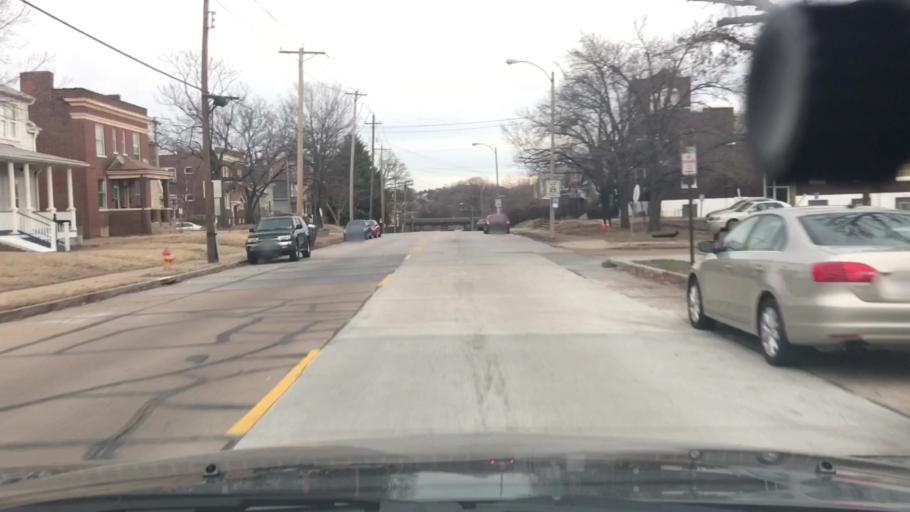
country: US
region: Missouri
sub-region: Saint Louis County
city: Maplewood
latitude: 38.6132
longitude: -90.3133
